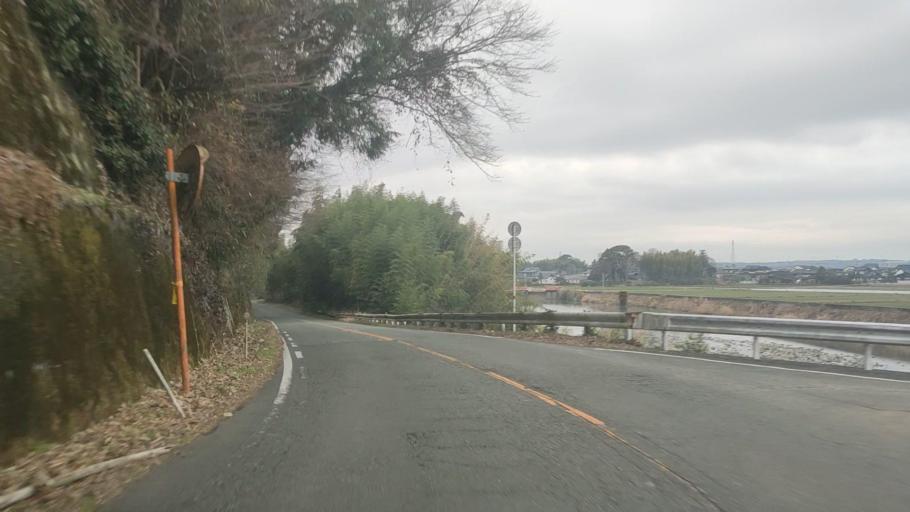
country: JP
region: Kumamoto
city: Ozu
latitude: 32.8529
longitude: 130.8658
